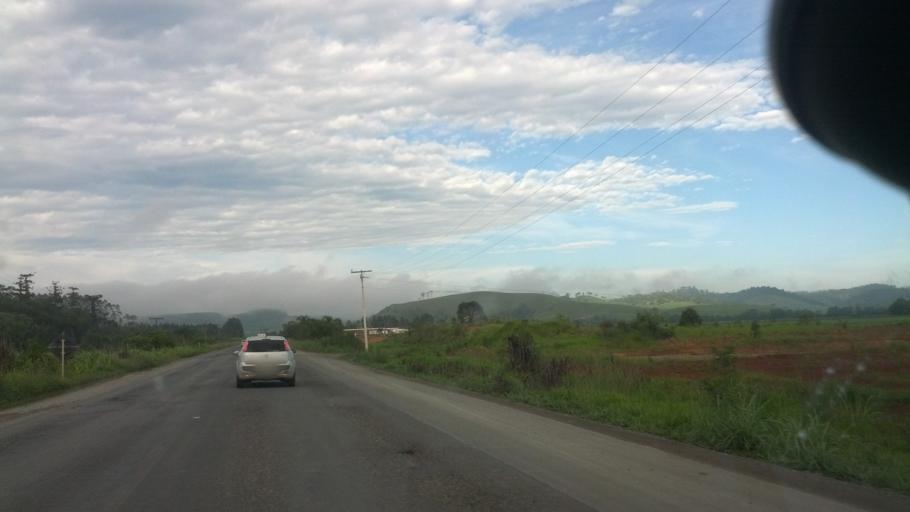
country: BR
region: Santa Catarina
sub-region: Otacilio Costa
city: Otacilio Costa
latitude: -27.2481
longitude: -49.9813
